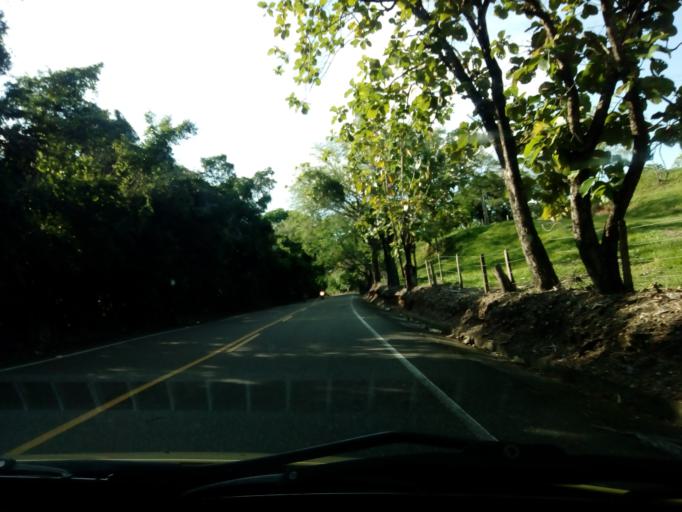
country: CO
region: Boyaca
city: Puerto Boyaca
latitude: 5.9334
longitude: -74.5384
